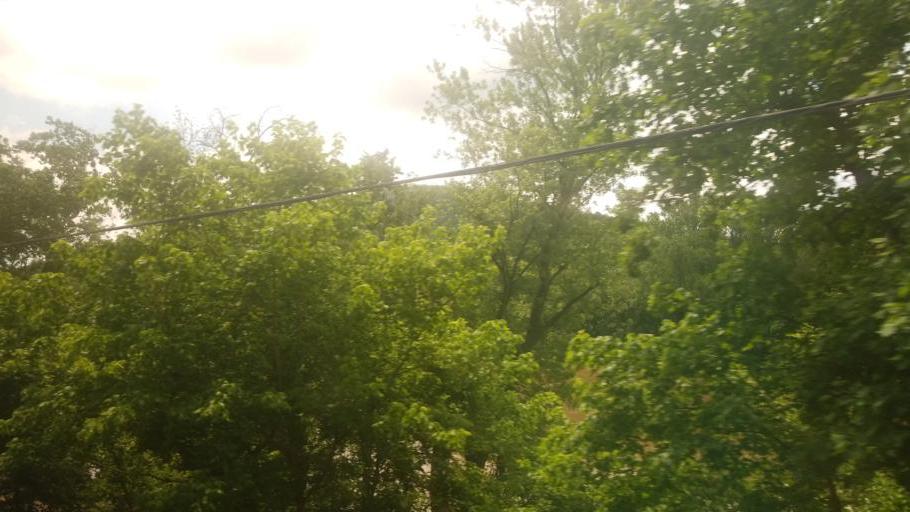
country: US
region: Maryland
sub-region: Frederick County
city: Point of Rocks
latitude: 39.2757
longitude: -77.5448
